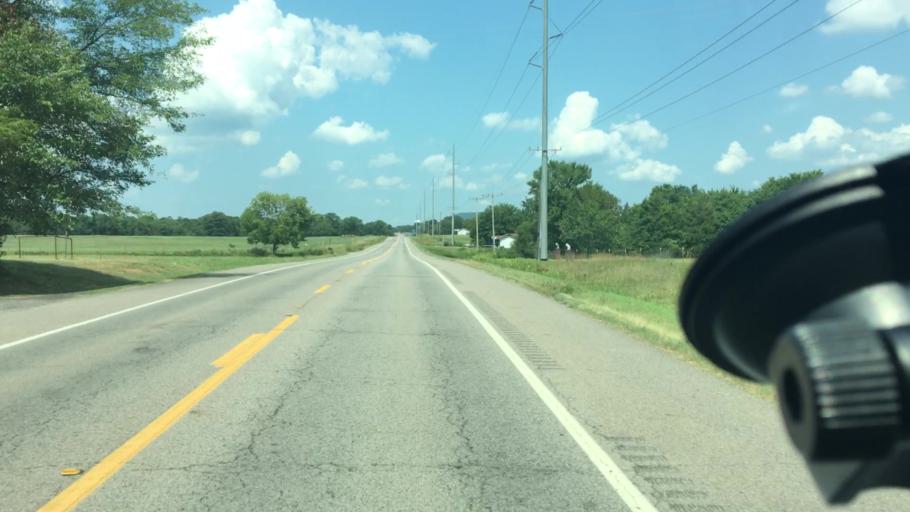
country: US
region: Arkansas
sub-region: Logan County
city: Paris
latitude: 35.2949
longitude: -93.6676
